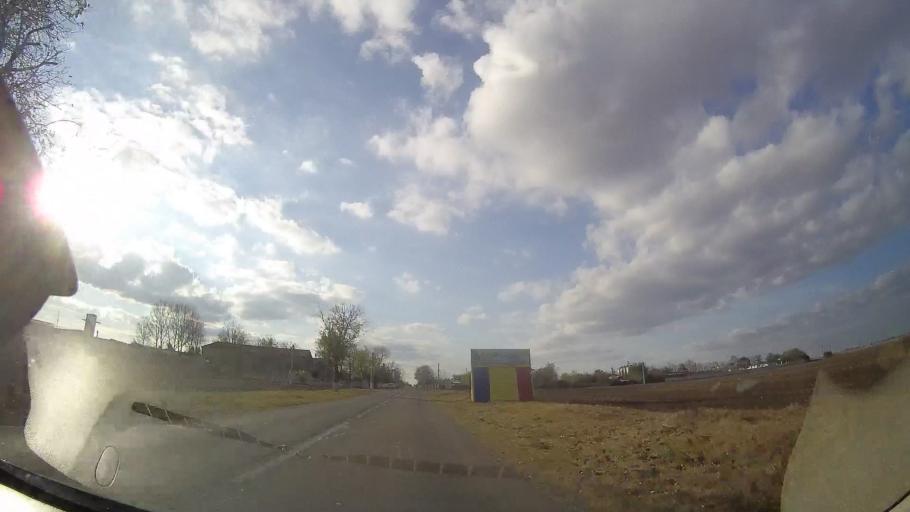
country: RO
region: Constanta
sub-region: Comuna Negru Voda
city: Negru Voda
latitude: 43.8194
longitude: 28.2306
